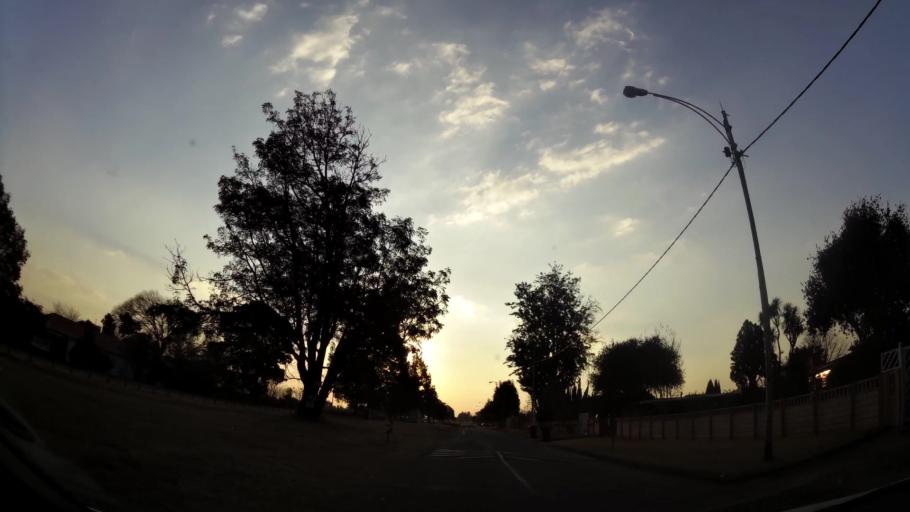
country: ZA
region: Gauteng
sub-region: Ekurhuleni Metropolitan Municipality
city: Springs
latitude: -26.2651
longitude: 28.4013
